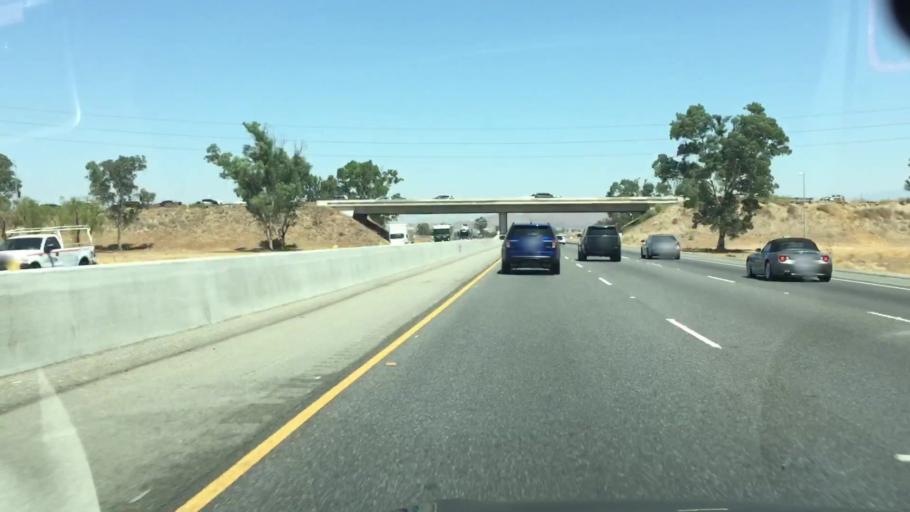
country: US
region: California
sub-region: Riverside County
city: Sun City
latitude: 33.6402
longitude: -117.1711
